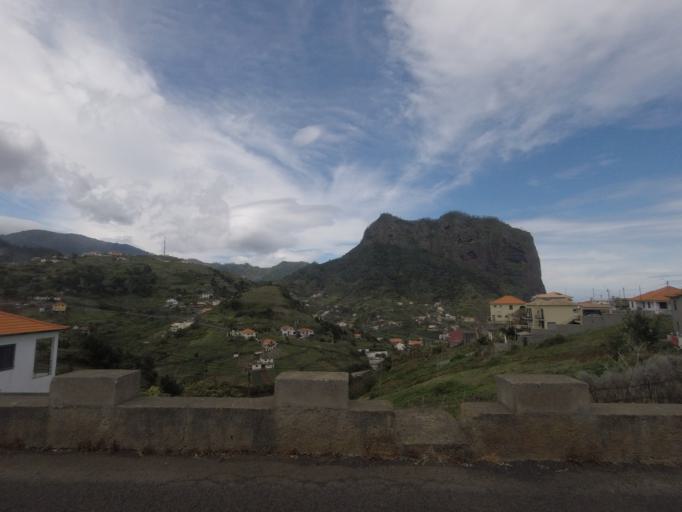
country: PT
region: Madeira
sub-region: Santana
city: Santana
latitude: 32.7665
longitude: -16.8260
